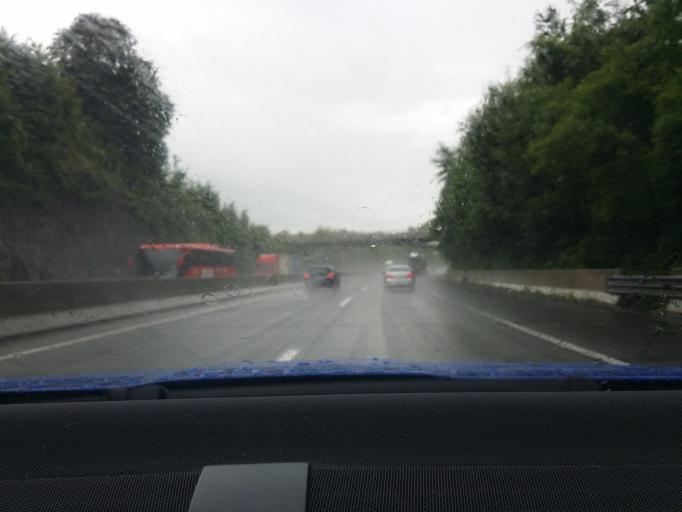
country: AT
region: Salzburg
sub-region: Politischer Bezirk Hallein
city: Kuchl
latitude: 47.6299
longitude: 13.1318
